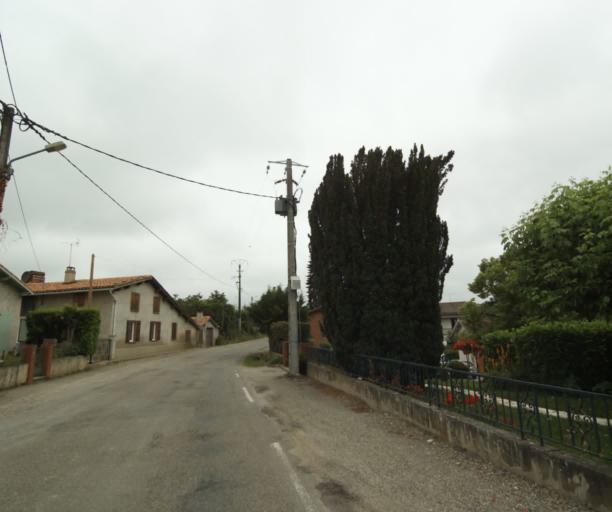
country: FR
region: Midi-Pyrenees
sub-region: Departement du Tarn-et-Garonne
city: Montbeton
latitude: 43.9896
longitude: 1.3081
